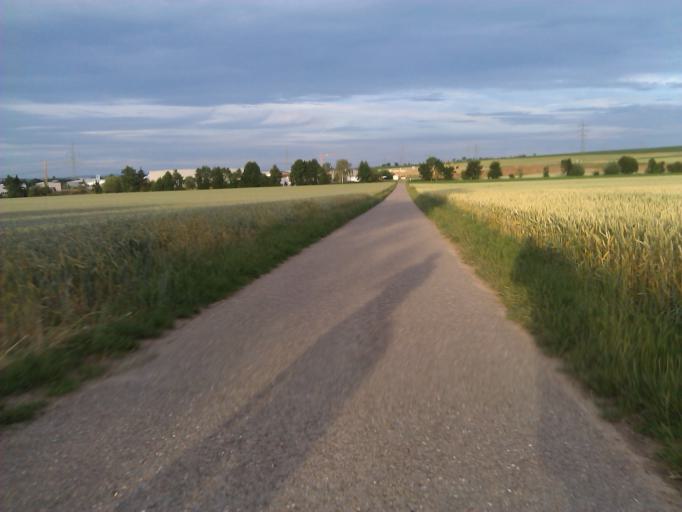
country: DE
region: Baden-Wuerttemberg
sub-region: Regierungsbezirk Stuttgart
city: Cleebronn
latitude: 49.0648
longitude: 9.0333
